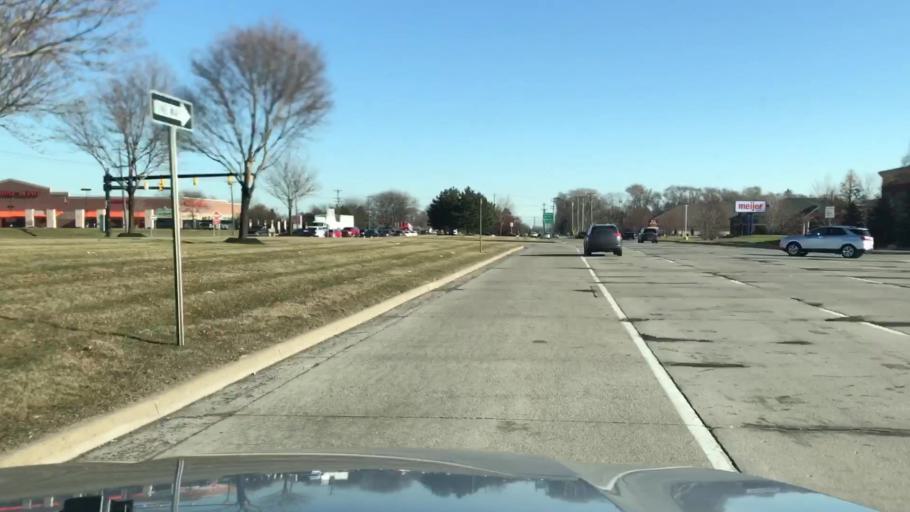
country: US
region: Michigan
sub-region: Macomb County
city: Sterling Heights
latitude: 42.5655
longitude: -83.0286
